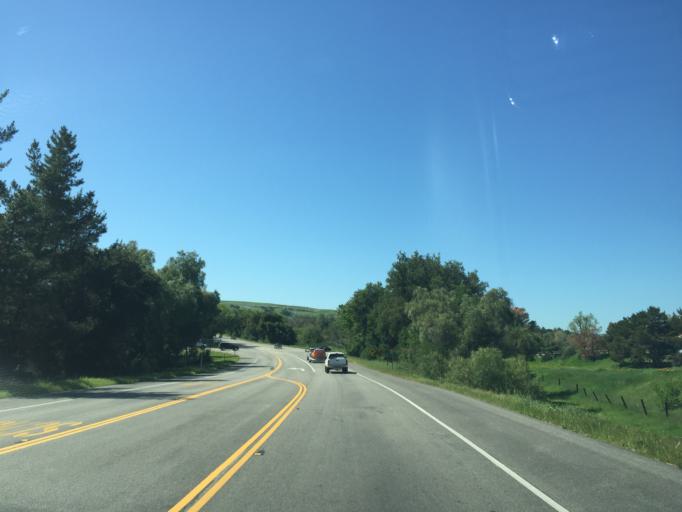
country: US
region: California
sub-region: Santa Barbara County
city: Los Olivos
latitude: 34.6675
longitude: -120.1134
